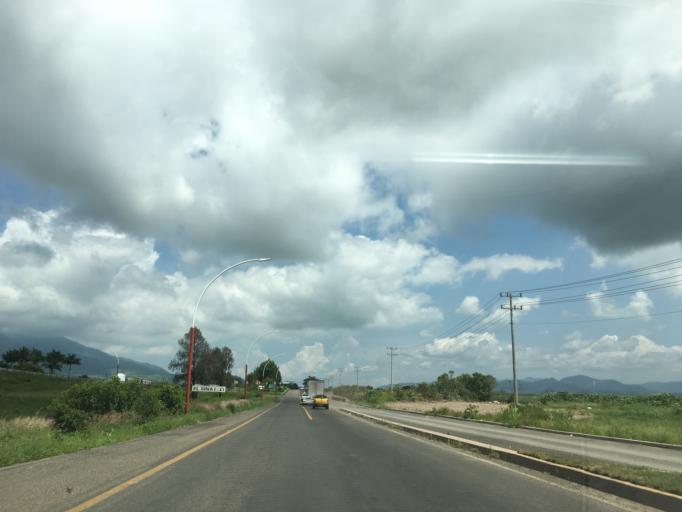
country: MX
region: Nayarit
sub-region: Tepic
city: La Corregidora
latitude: 21.4646
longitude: -104.8333
